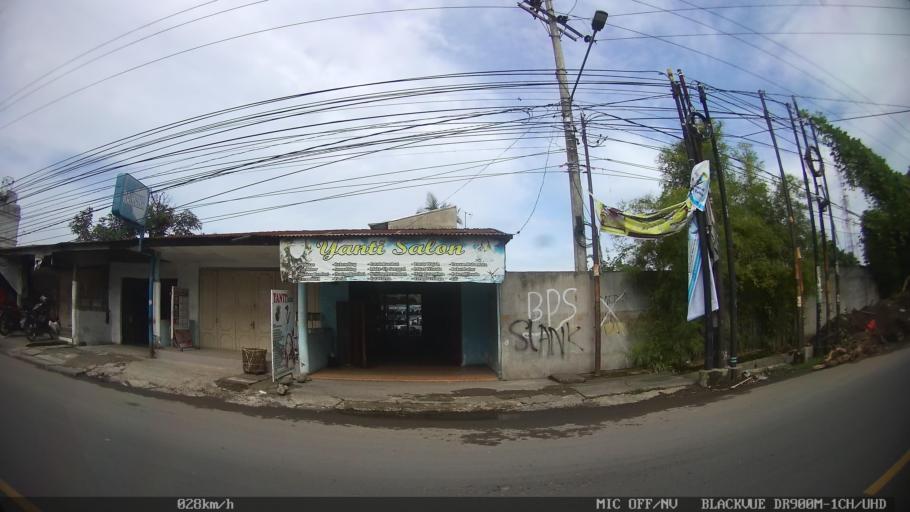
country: ID
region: North Sumatra
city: Medan
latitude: 3.6265
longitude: 98.7076
